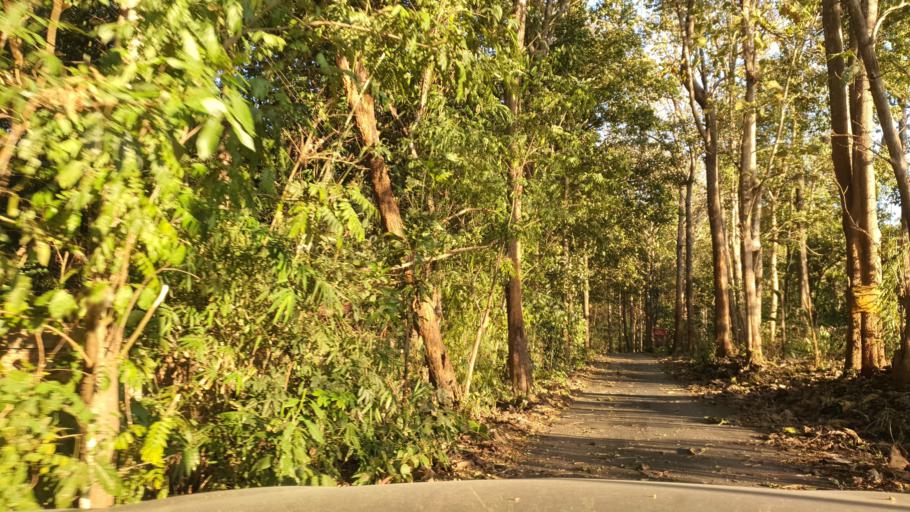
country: TH
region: Chiang Mai
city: Mae Wang
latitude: 18.6598
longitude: 98.6416
